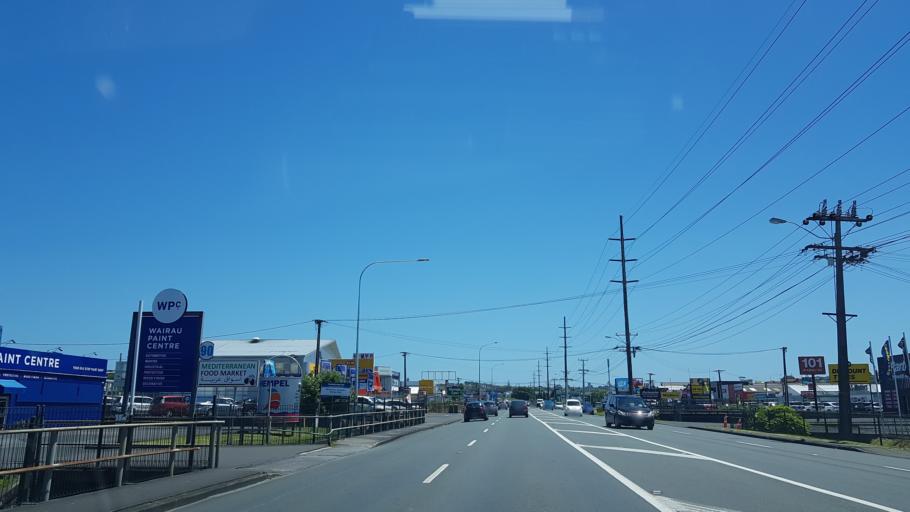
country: NZ
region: Auckland
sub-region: Auckland
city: North Shore
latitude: -36.7757
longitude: 174.7433
